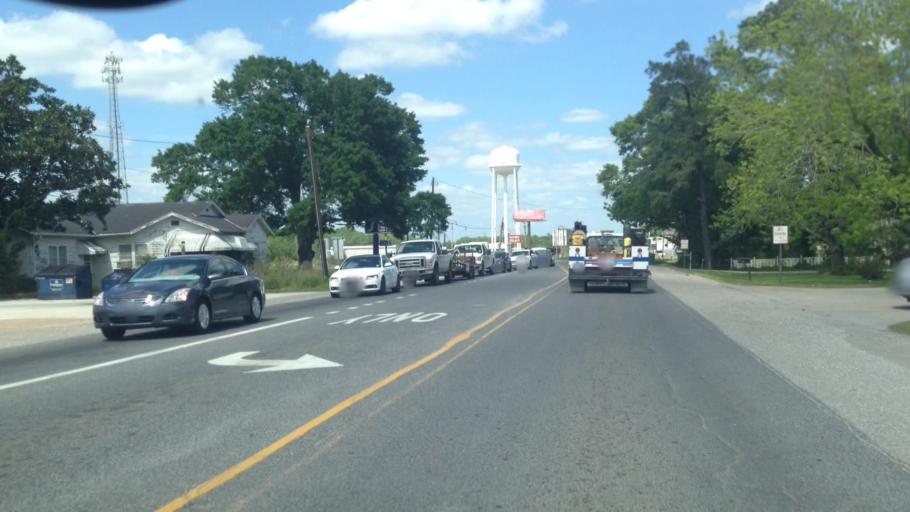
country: US
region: Louisiana
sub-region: Terrebonne Parish
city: Houma
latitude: 29.6455
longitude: -90.6875
